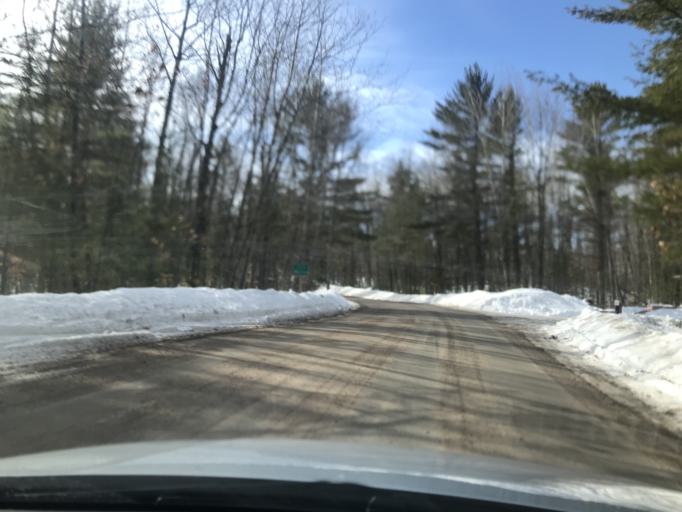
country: US
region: Wisconsin
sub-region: Menominee County
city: Legend Lake
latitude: 45.1168
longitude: -88.4334
